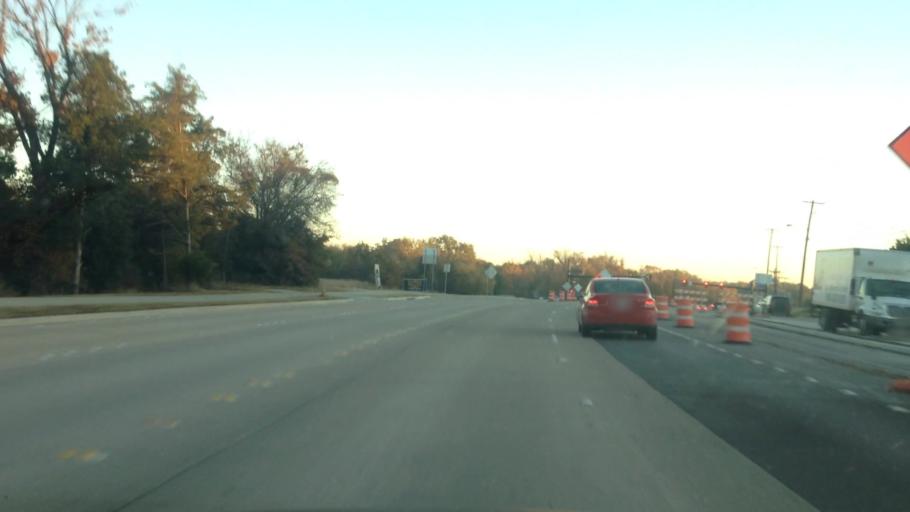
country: US
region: Texas
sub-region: Tarrant County
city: Southlake
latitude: 32.9094
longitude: -97.1366
